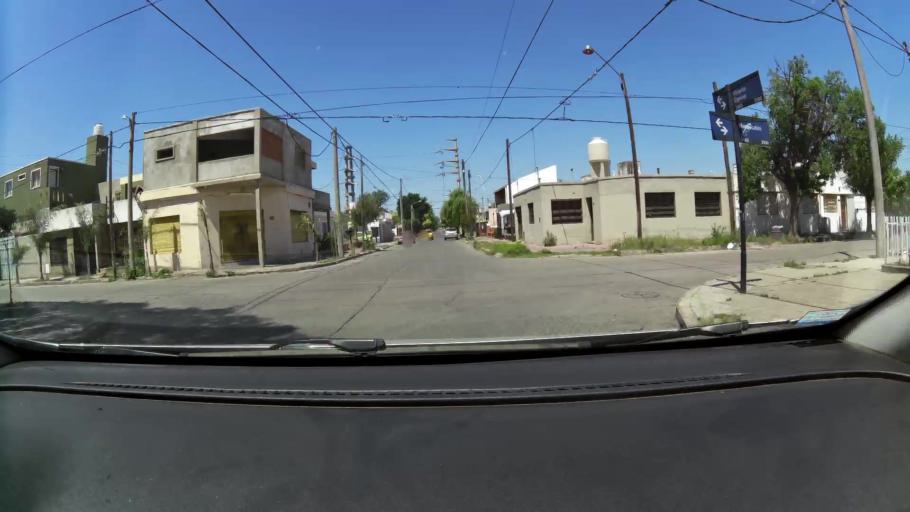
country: AR
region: Cordoba
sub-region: Departamento de Capital
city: Cordoba
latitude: -31.3782
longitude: -64.1998
